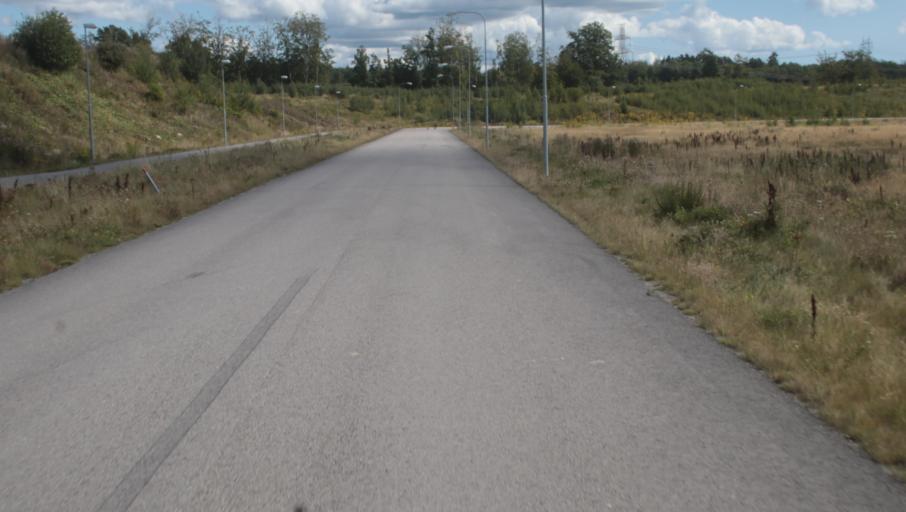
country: SE
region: Blekinge
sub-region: Karlshamns Kommun
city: Karlshamn
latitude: 56.1663
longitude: 14.8305
